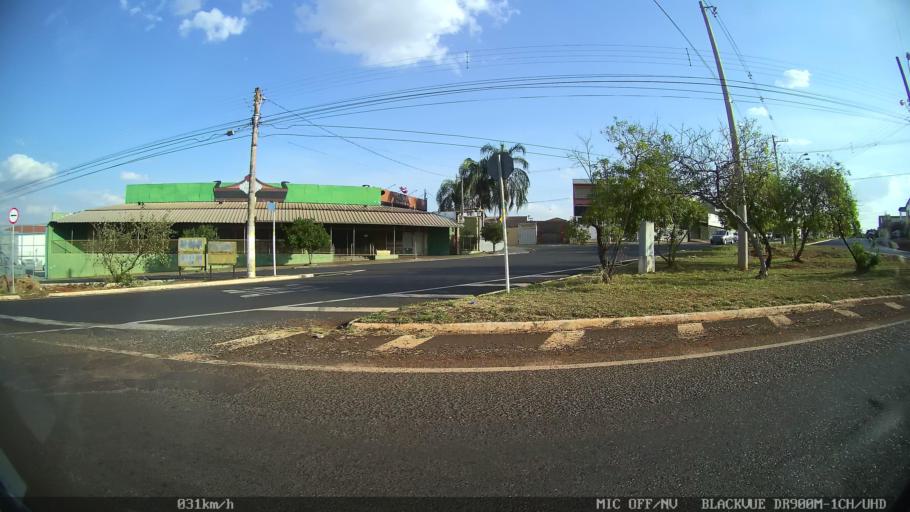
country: BR
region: Sao Paulo
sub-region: Ribeirao Preto
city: Ribeirao Preto
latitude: -21.1397
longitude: -47.8347
